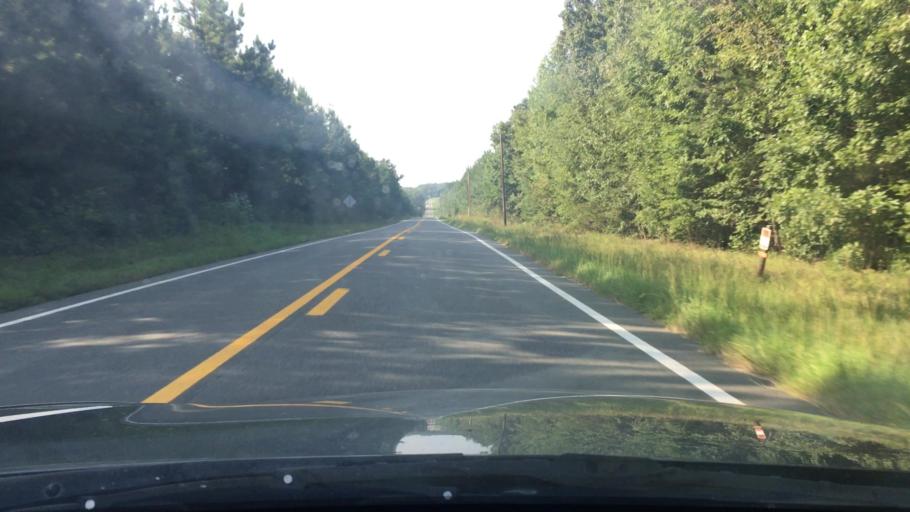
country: US
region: North Carolina
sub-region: Alamance County
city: Green Level
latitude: 36.2418
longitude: -79.3227
